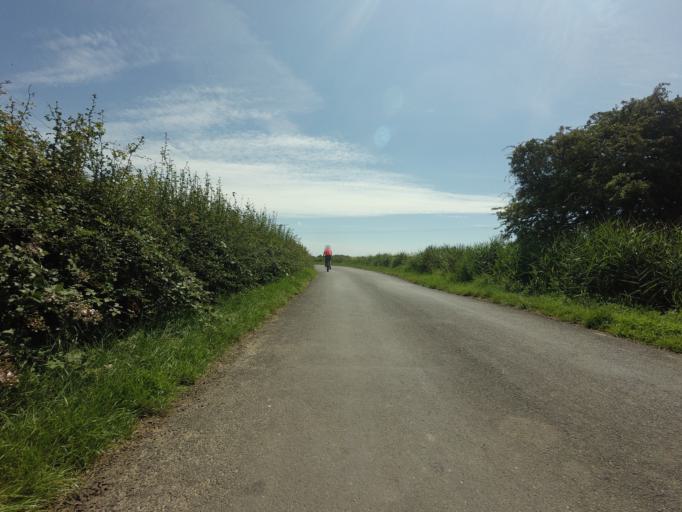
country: GB
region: England
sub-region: Kent
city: Lydd
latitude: 50.9781
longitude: 0.8492
